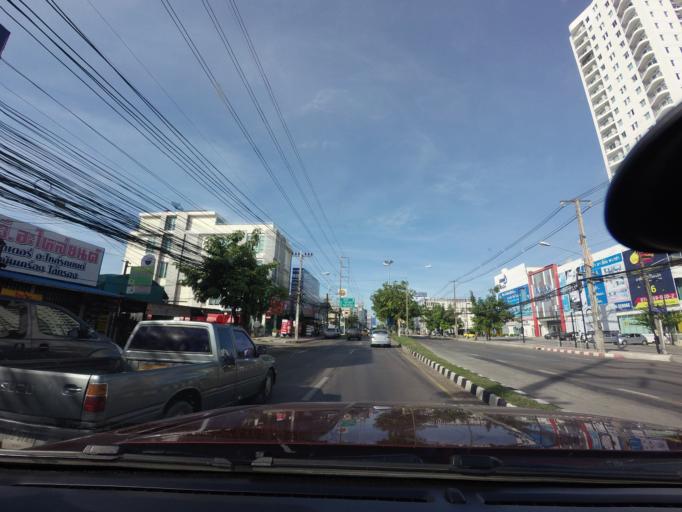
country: TH
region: Songkhla
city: Hat Yai
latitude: 6.9944
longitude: 100.4865
